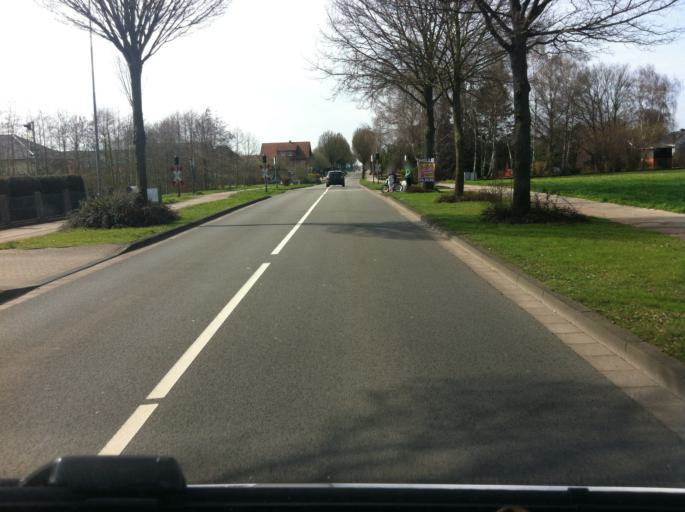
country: DE
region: North Rhine-Westphalia
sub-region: Regierungsbezirk Detmold
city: Minden
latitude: 52.2992
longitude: 8.8729
